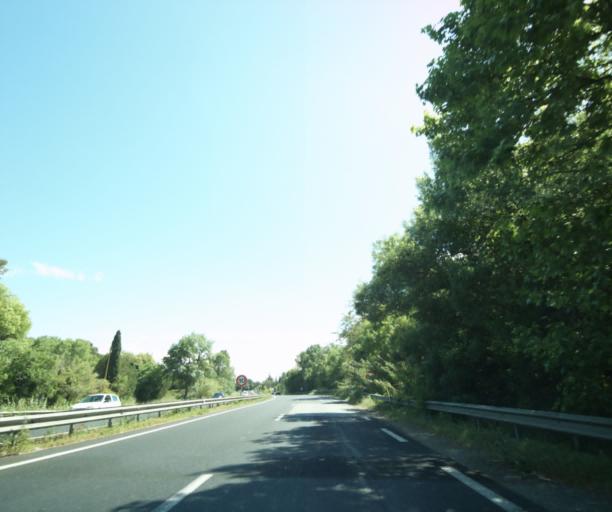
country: FR
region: Languedoc-Roussillon
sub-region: Departement de l'Herault
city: Laverune
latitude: 43.5971
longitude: 3.8199
